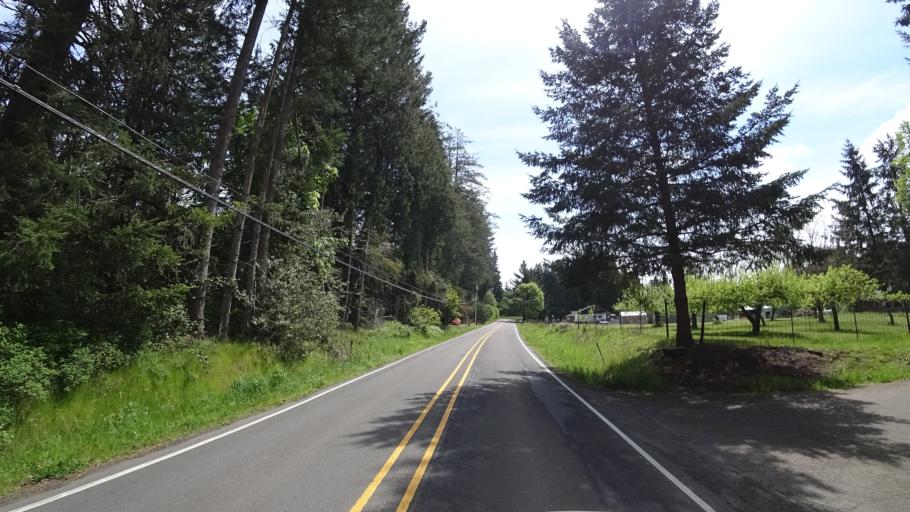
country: US
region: Oregon
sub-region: Washington County
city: Hillsboro
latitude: 45.5423
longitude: -123.0028
